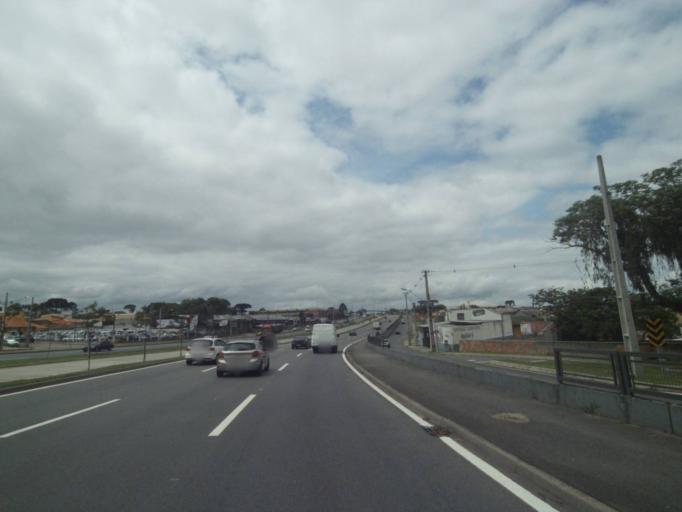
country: BR
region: Parana
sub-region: Curitiba
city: Curitiba
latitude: -25.4350
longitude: -49.2334
